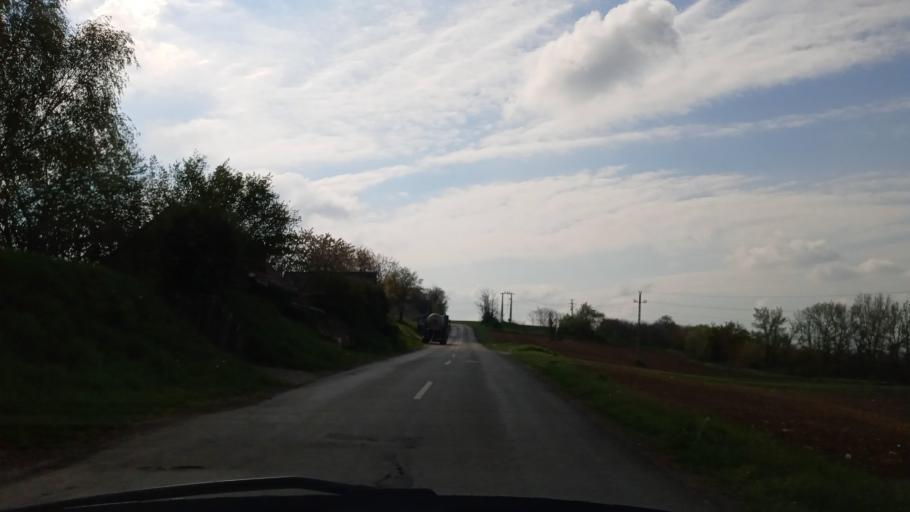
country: HU
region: Baranya
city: Pecsvarad
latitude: 46.1570
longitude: 18.4356
